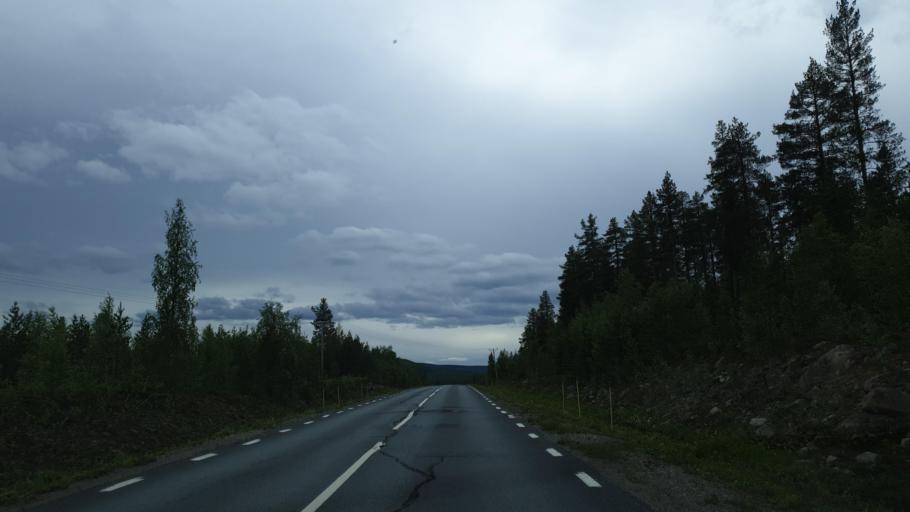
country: SE
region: Vaesterbotten
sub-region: Sorsele Kommun
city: Sorsele
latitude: 65.5348
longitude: 17.3954
